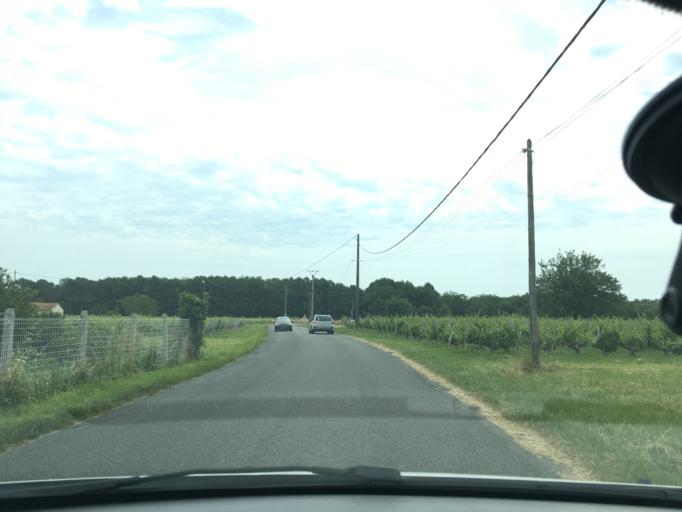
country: FR
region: Aquitaine
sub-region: Departement de la Gironde
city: Gaillan-en-Medoc
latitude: 45.3359
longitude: -0.9842
